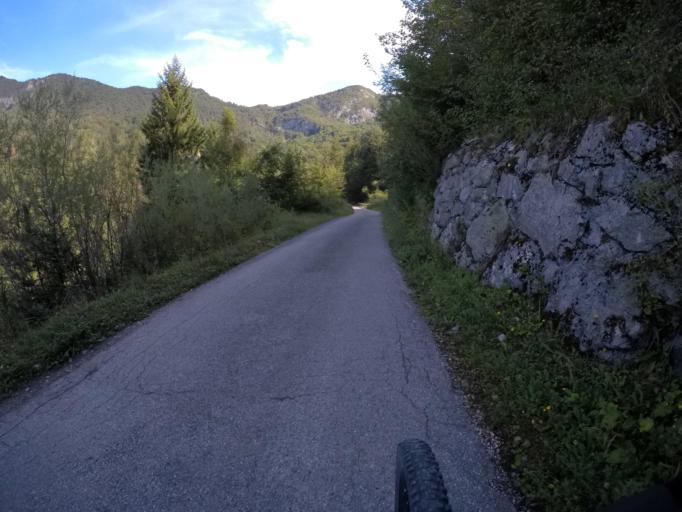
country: IT
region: Friuli Venezia Giulia
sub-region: Provincia di Udine
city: Zuglio
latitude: 46.4338
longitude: 13.0669
